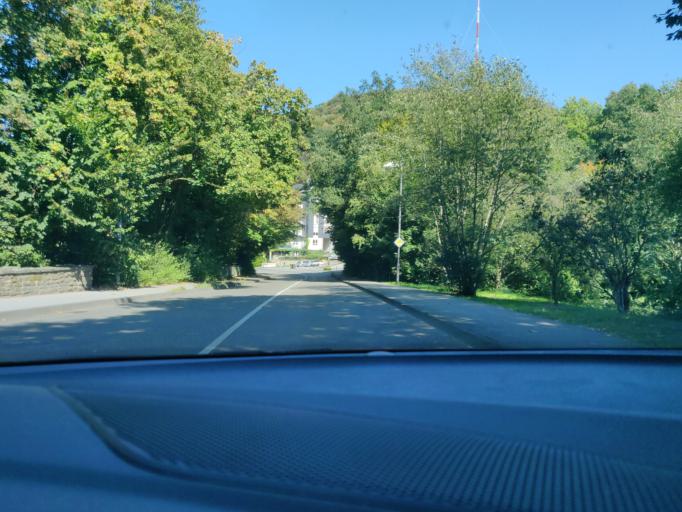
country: DE
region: North Rhine-Westphalia
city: Hattingen
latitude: 51.3493
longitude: 7.1239
